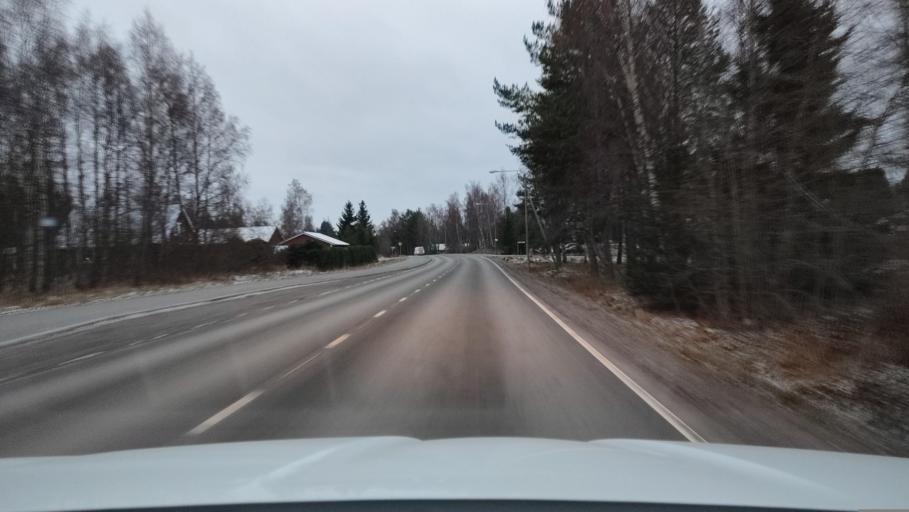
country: FI
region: Ostrobothnia
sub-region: Vaasa
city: Replot
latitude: 63.2248
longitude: 21.4113
